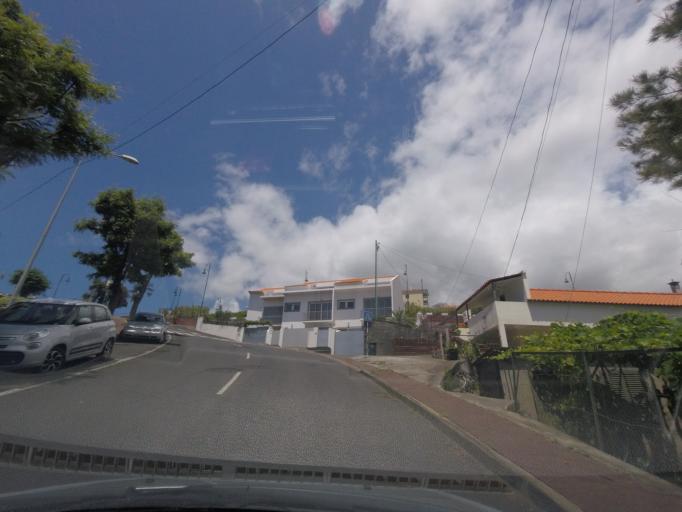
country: PT
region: Madeira
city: Canico
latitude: 32.6451
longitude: -16.8383
